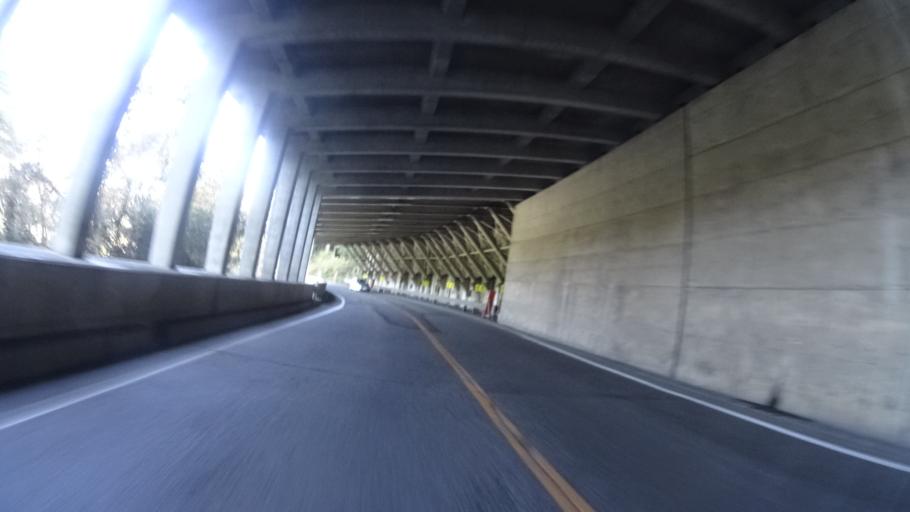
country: JP
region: Ishikawa
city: Tsurugi-asahimachi
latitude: 36.3695
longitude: 136.6135
